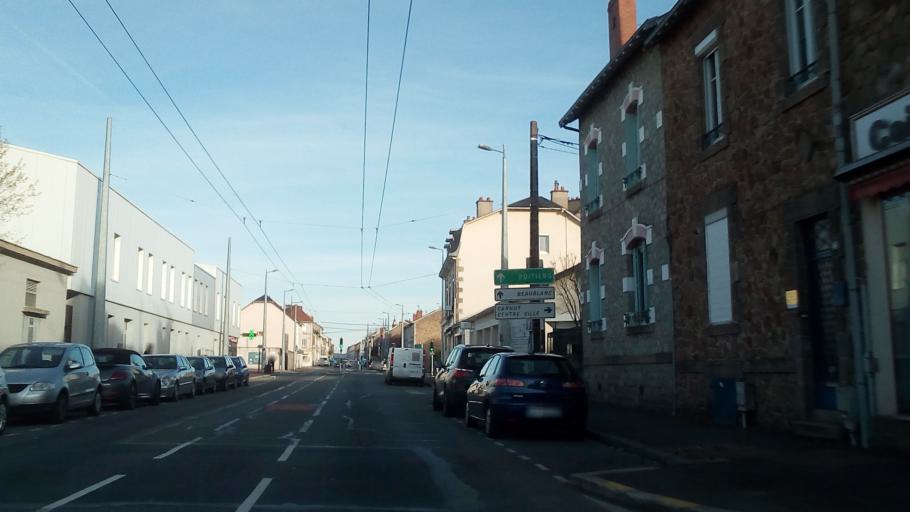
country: FR
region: Limousin
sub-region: Departement de la Haute-Vienne
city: Limoges
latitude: 45.8435
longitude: 1.2457
